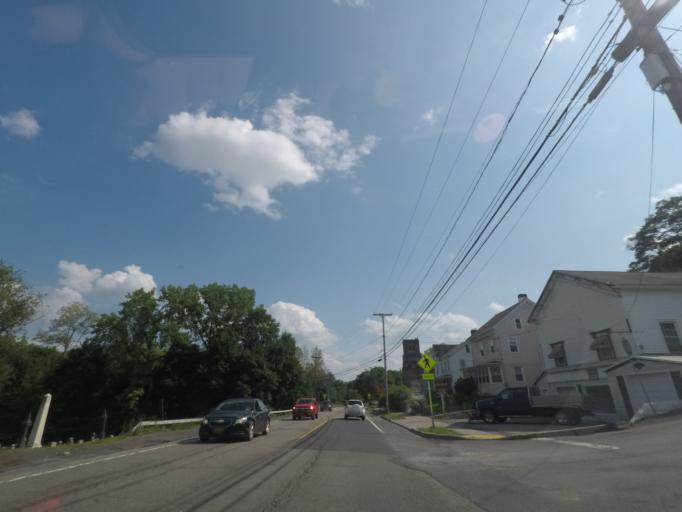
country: US
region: New York
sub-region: Ulster County
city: Marlboro
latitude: 41.6024
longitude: -73.9724
